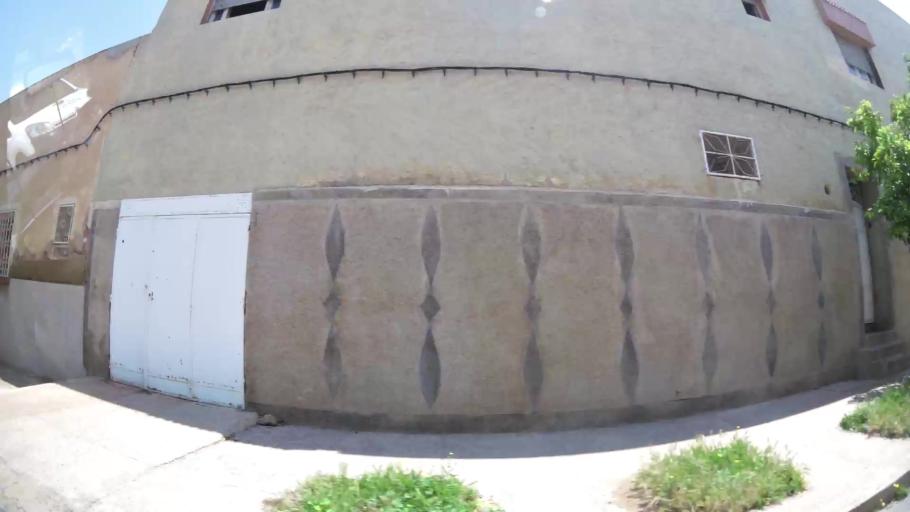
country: MA
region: Oriental
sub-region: Oujda-Angad
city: Oujda
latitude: 34.6817
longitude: -1.8879
